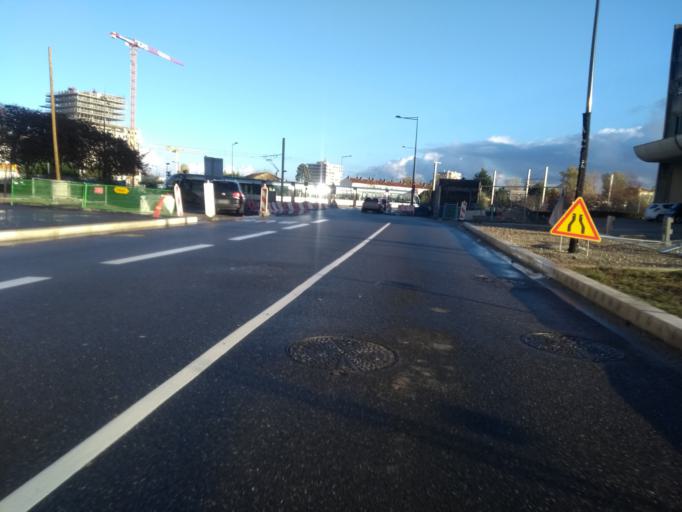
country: FR
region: Aquitaine
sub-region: Departement de la Gironde
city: Begles
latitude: 44.8211
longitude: -0.5512
